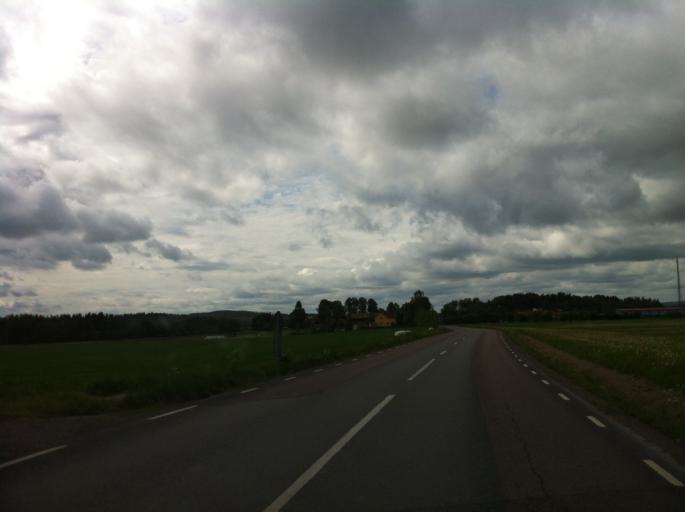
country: SE
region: Vaermland
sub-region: Sunne Kommun
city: Sunne
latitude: 59.8596
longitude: 13.1649
